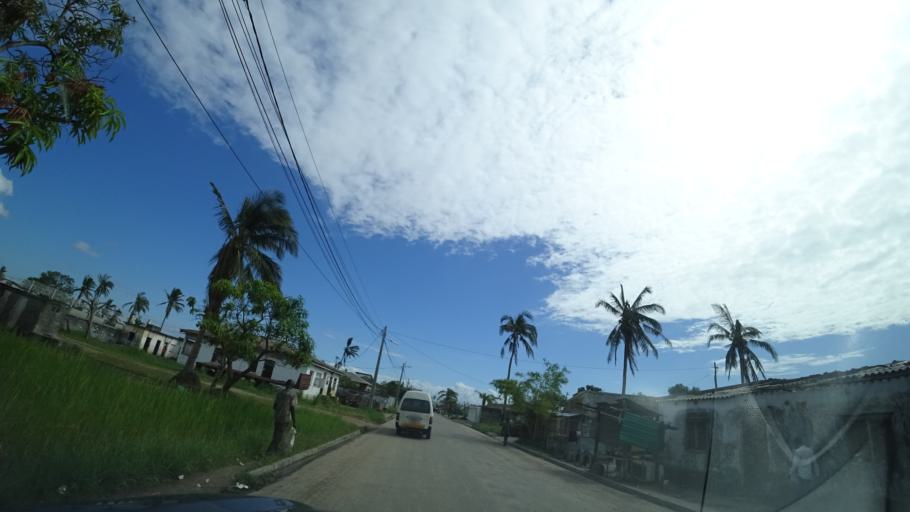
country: MZ
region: Sofala
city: Beira
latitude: -19.7556
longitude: 34.8628
